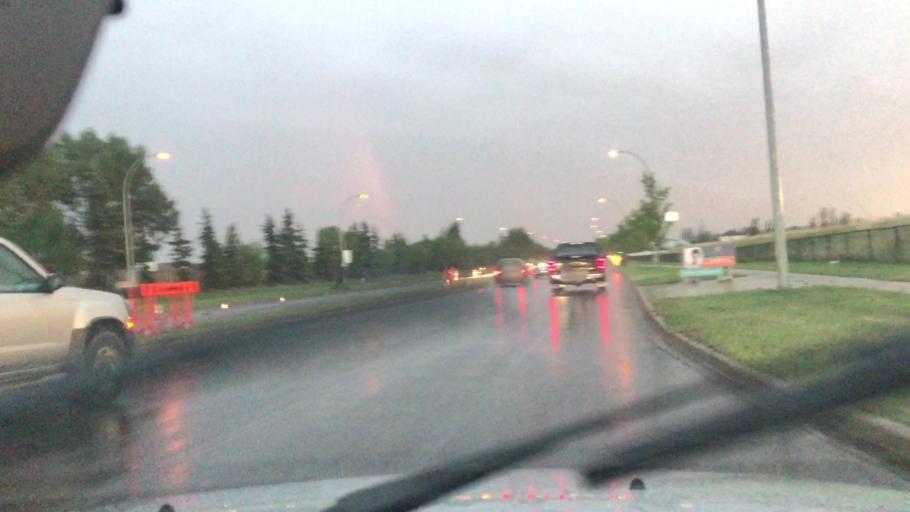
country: CA
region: Alberta
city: St. Albert
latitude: 53.6283
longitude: -113.5417
